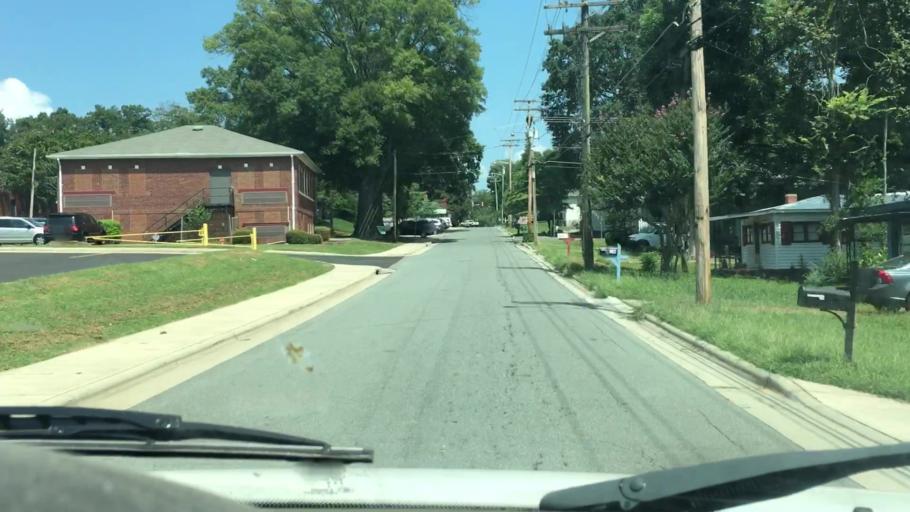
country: US
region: North Carolina
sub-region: Mecklenburg County
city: Cornelius
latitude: 35.4808
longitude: -80.8637
